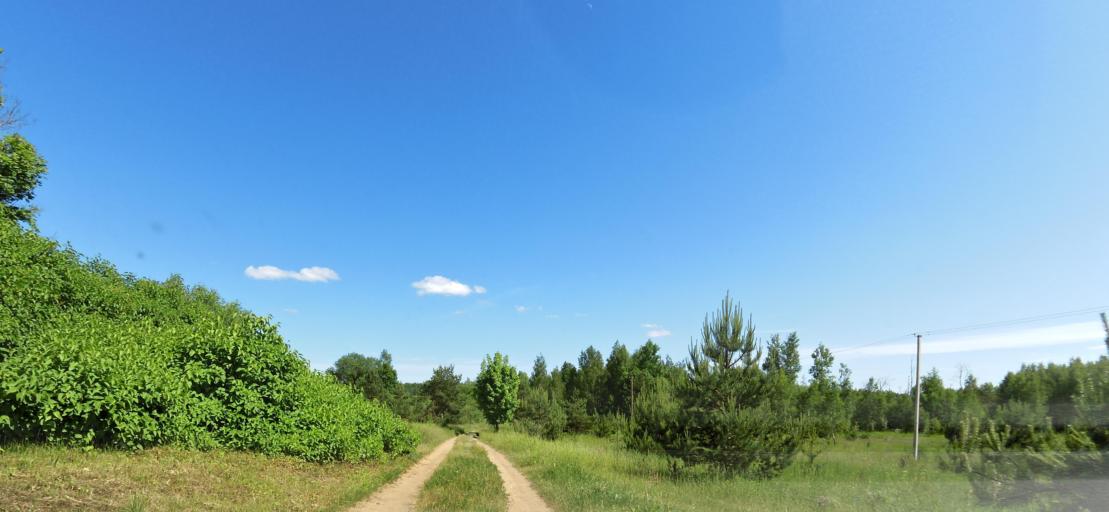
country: LT
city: Sirvintos
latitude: 55.2570
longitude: 25.1010
